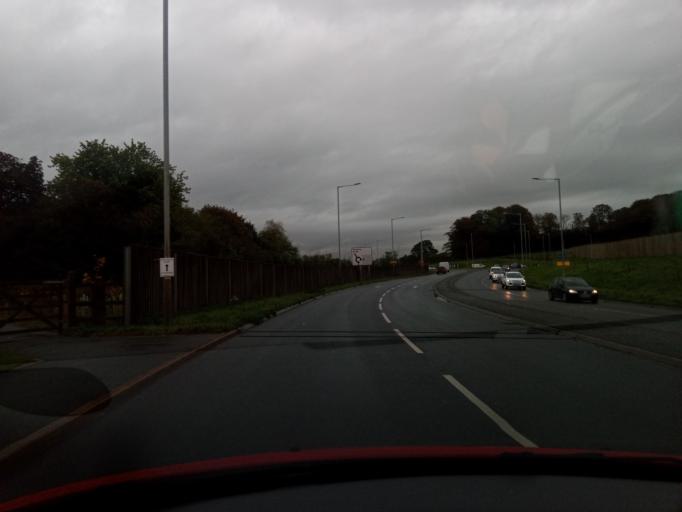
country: GB
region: England
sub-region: Lancashire
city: Preston
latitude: 53.8027
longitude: -2.7166
